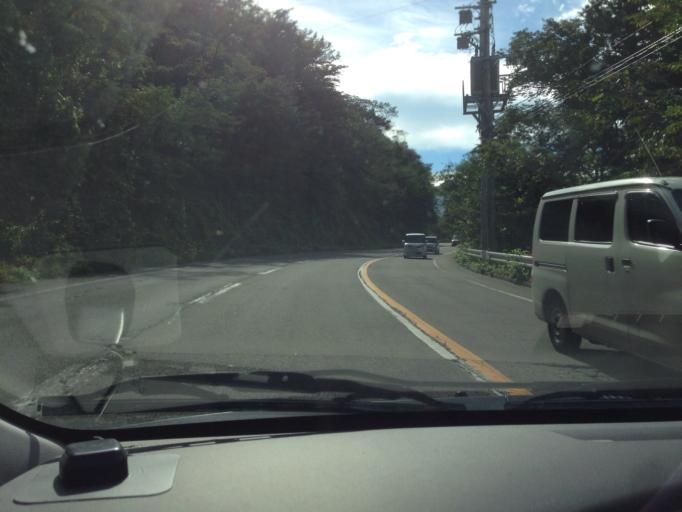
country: JP
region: Fukushima
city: Fukushima-shi
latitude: 37.6938
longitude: 140.3443
